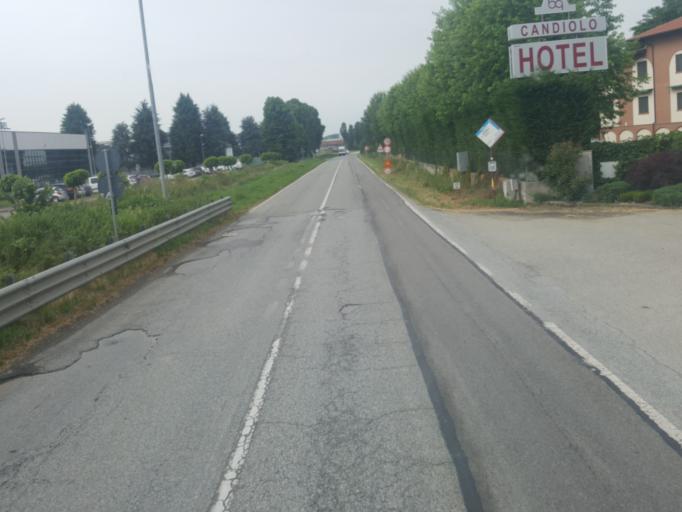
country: IT
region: Piedmont
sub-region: Provincia di Torino
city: Candiolo
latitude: 44.9604
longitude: 7.5656
